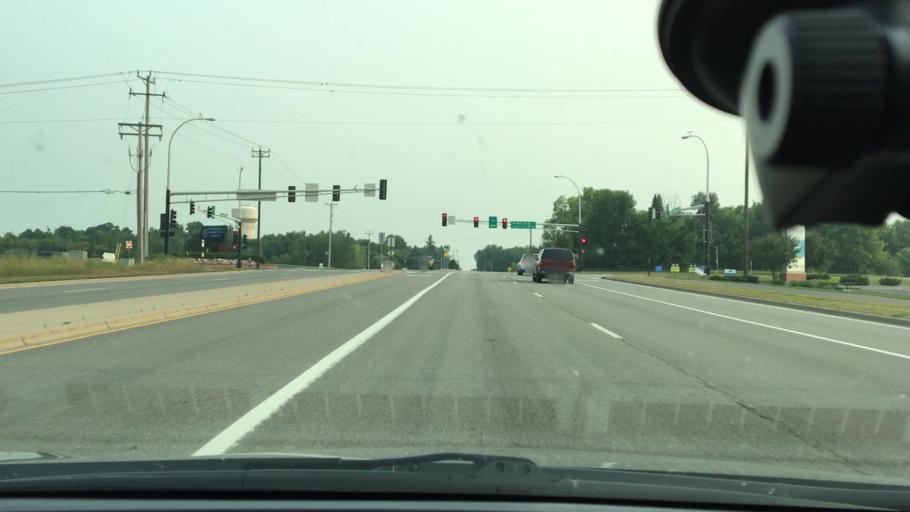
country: US
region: Minnesota
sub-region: Wright County
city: Saint Michael
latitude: 45.2254
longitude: -93.6646
